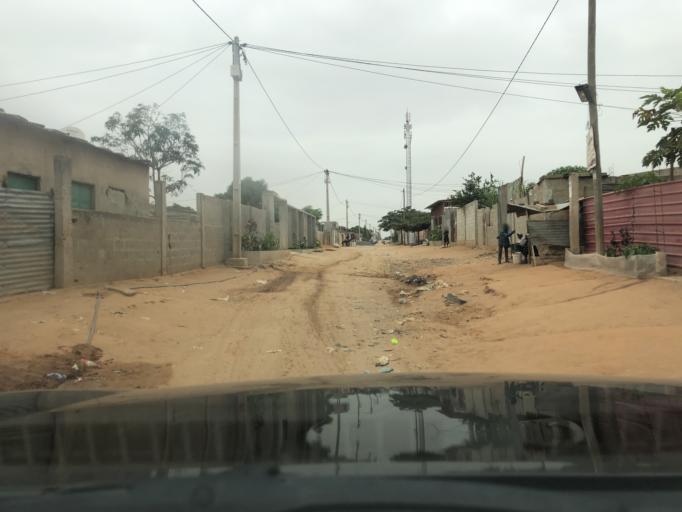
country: AO
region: Luanda
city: Luanda
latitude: -8.9386
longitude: 13.2375
